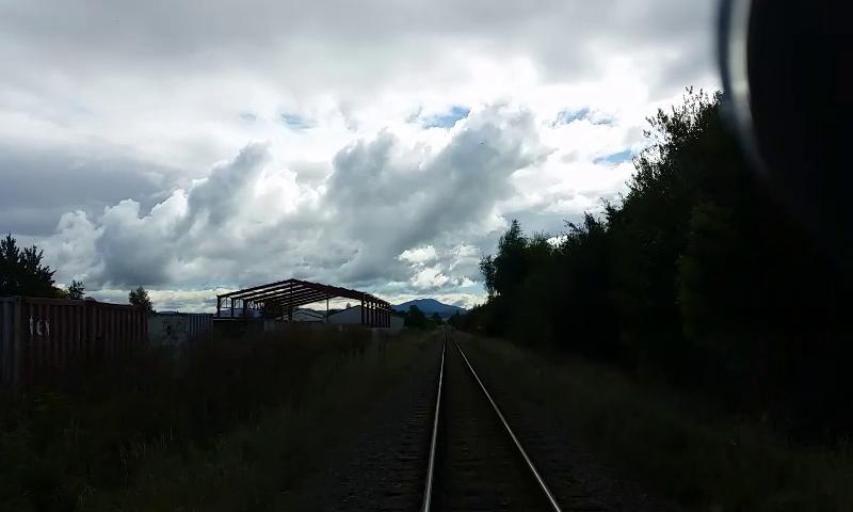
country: NZ
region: Canterbury
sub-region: Waimakariri District
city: Woodend
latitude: -43.3145
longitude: 172.6011
